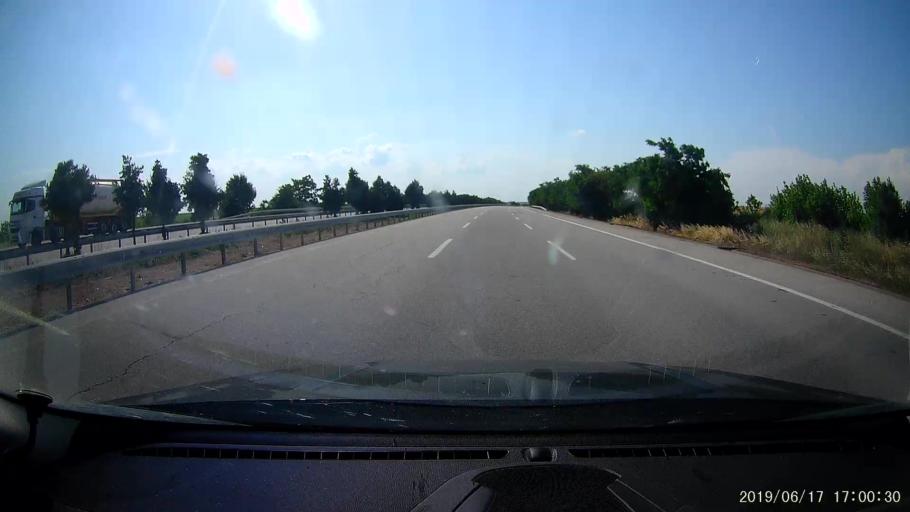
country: TR
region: Edirne
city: Haskoy
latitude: 41.6213
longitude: 26.8293
